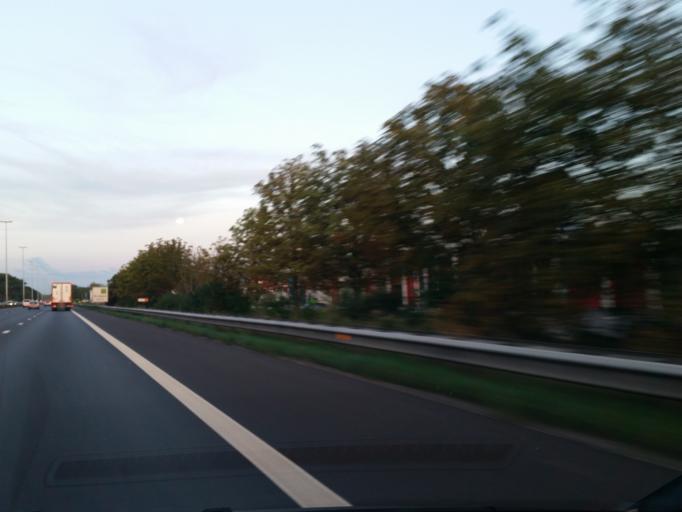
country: BE
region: Flanders
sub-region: Provincie Oost-Vlaanderen
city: Nevele
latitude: 51.0452
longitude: 3.5937
